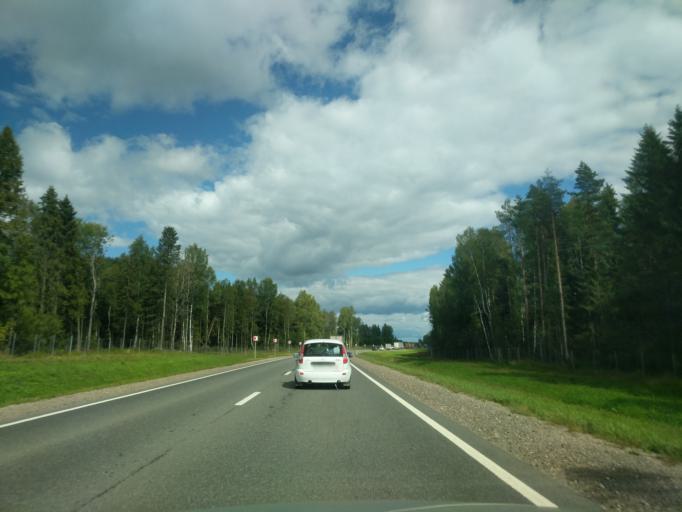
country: RU
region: Kostroma
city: Oktyabr'skiy
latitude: 57.8011
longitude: 41.2728
